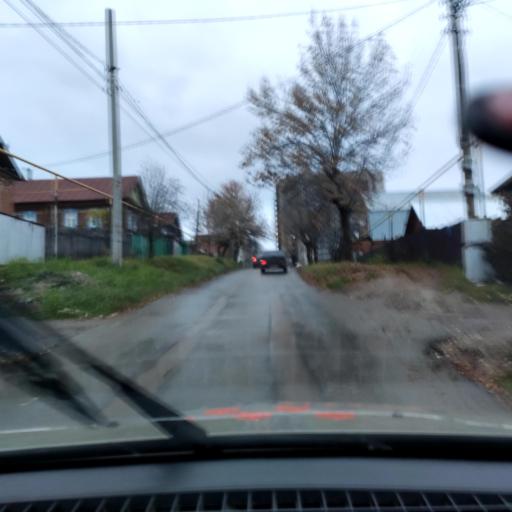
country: RU
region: Bashkortostan
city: Ufa
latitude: 54.7738
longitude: 56.0415
